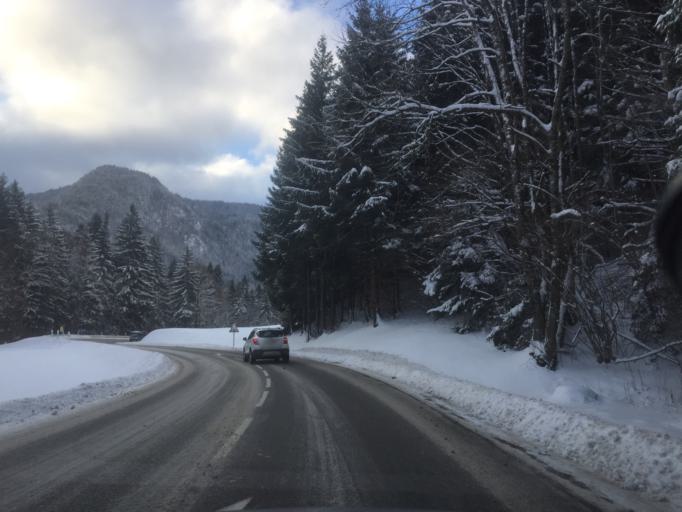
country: FR
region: Rhone-Alpes
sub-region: Departement de la Haute-Savoie
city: Abondance
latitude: 46.3031
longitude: 6.6751
